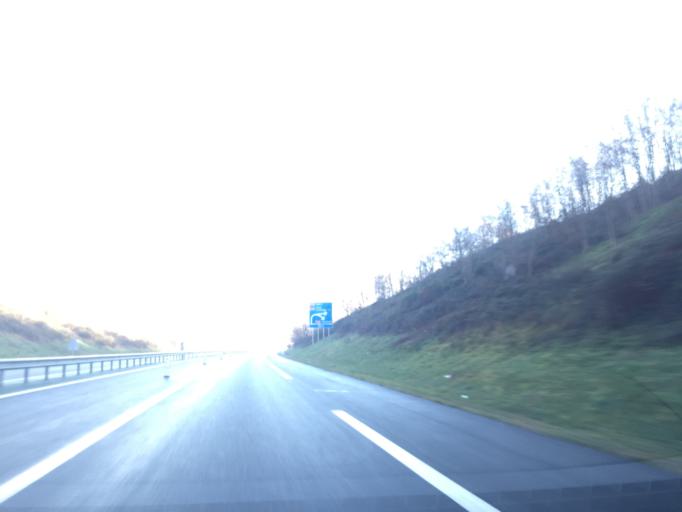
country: FR
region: Limousin
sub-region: Departement de la Correze
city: Varetz
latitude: 45.1859
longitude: 1.4800
